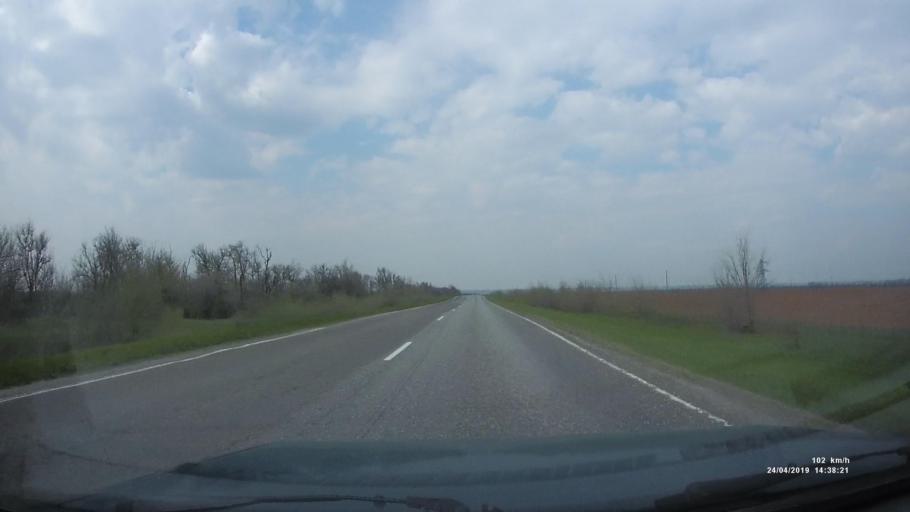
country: RU
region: Rostov
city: Remontnoye
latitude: 46.3999
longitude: 43.8861
